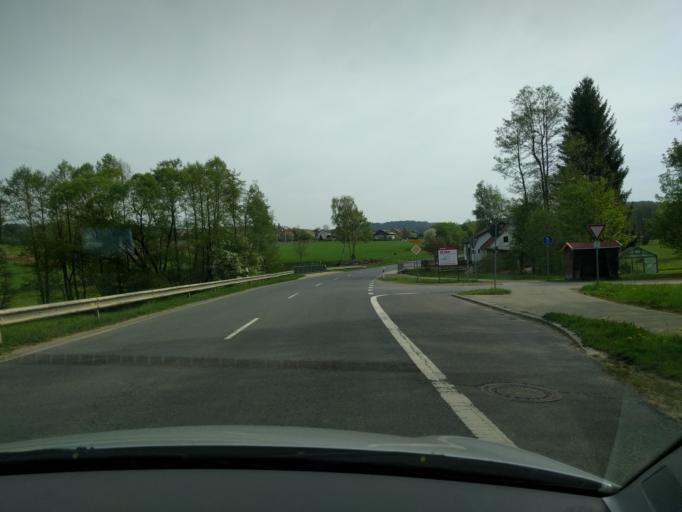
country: DE
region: Bavaria
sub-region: Upper Palatinate
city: Falkenstein
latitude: 49.1046
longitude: 12.4978
